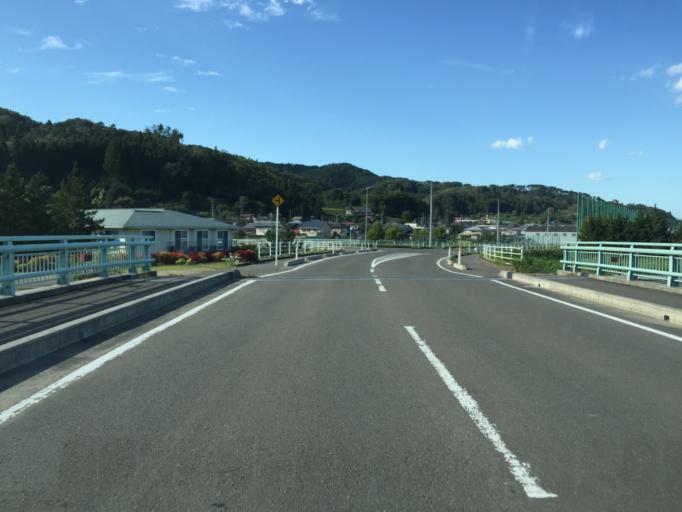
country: JP
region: Miyagi
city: Marumori
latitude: 37.9070
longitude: 140.7646
